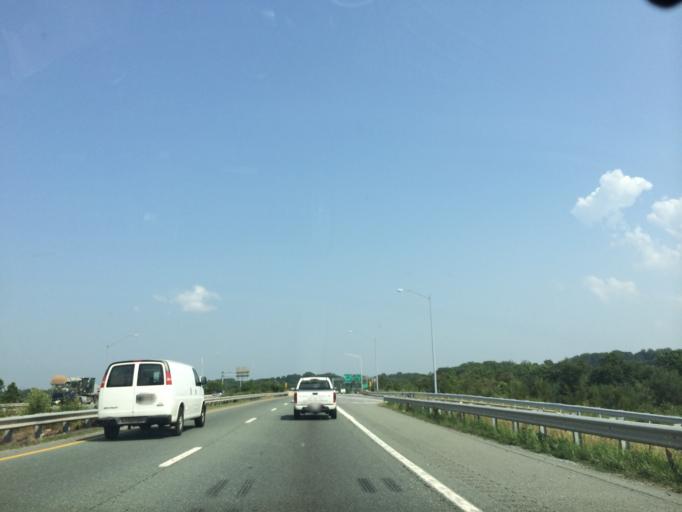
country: US
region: Maryland
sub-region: Howard County
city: Hanover
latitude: 39.1828
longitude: -76.7463
